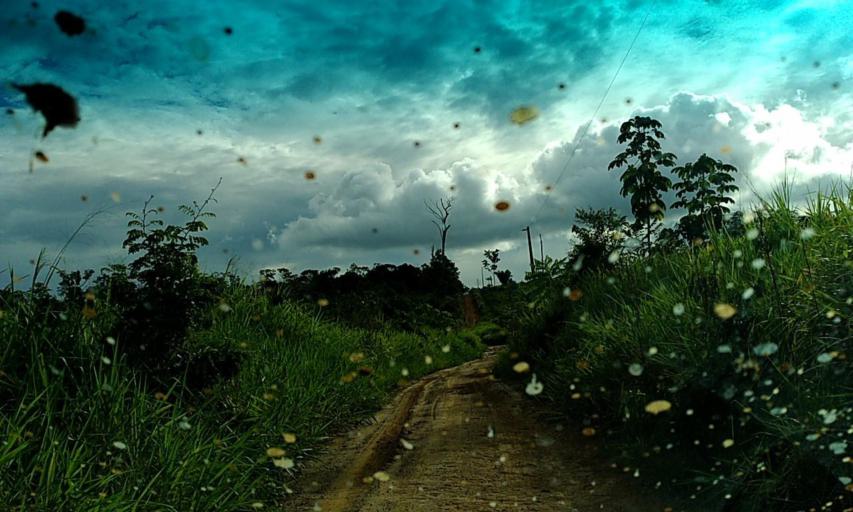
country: BR
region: Para
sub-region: Senador Jose Porfirio
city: Senador Jose Porfirio
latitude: -3.0053
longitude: -51.7419
